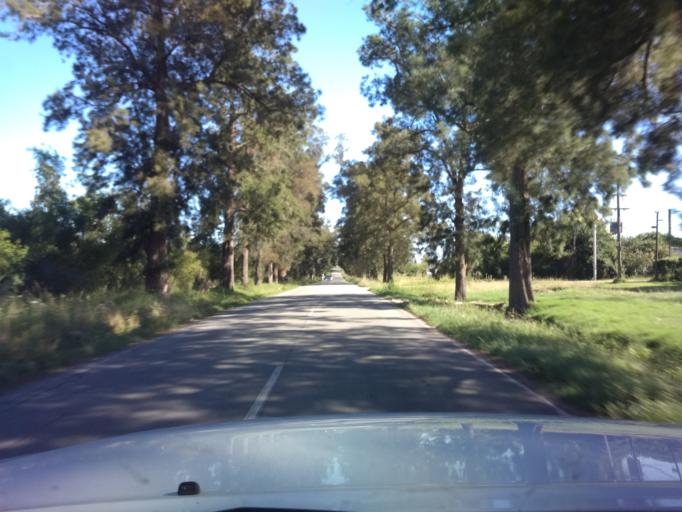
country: UY
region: Canelones
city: San Bautista
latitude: -34.3757
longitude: -55.9595
